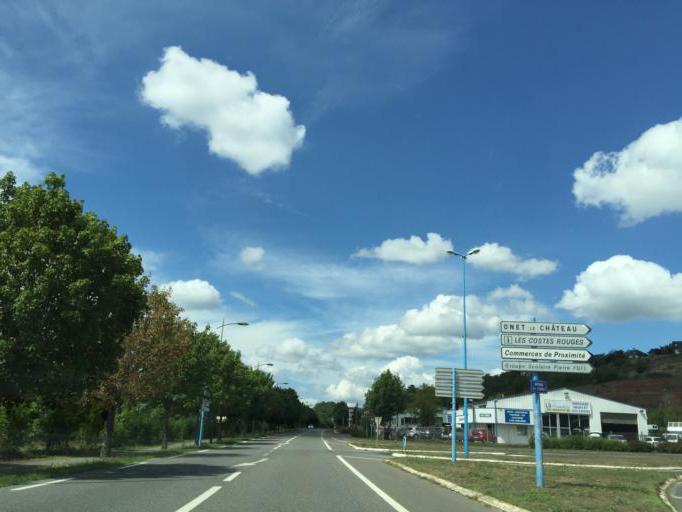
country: FR
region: Midi-Pyrenees
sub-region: Departement de l'Aveyron
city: Rodez
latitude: 44.3710
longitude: 2.5686
